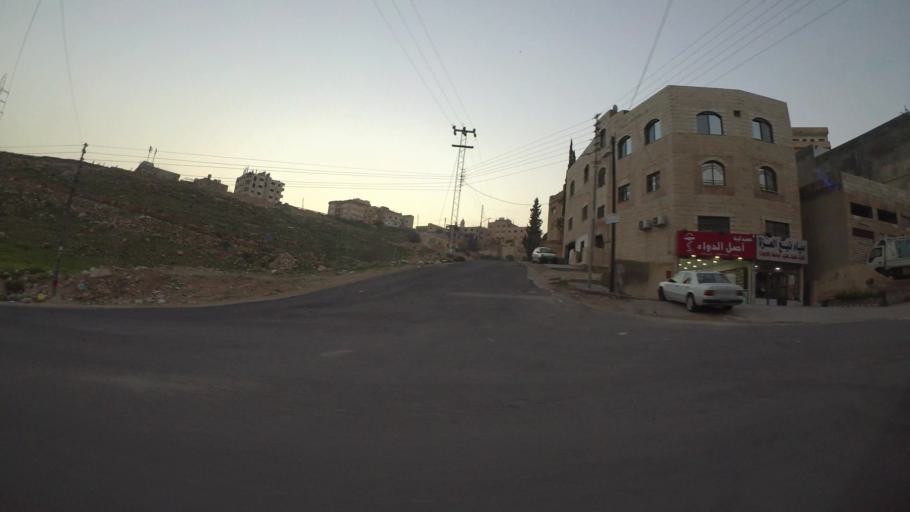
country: JO
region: Amman
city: Amman
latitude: 31.9945
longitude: 35.9767
